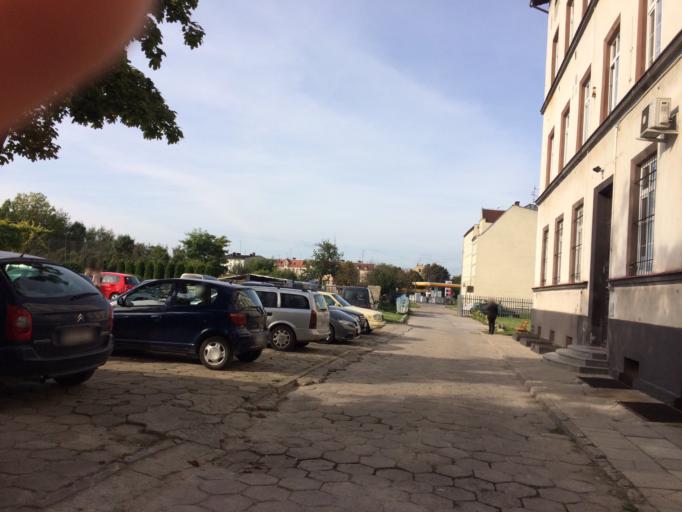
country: PL
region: Warmian-Masurian Voivodeship
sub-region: Powiat elblaski
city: Elblag
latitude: 54.1555
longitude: 19.4006
